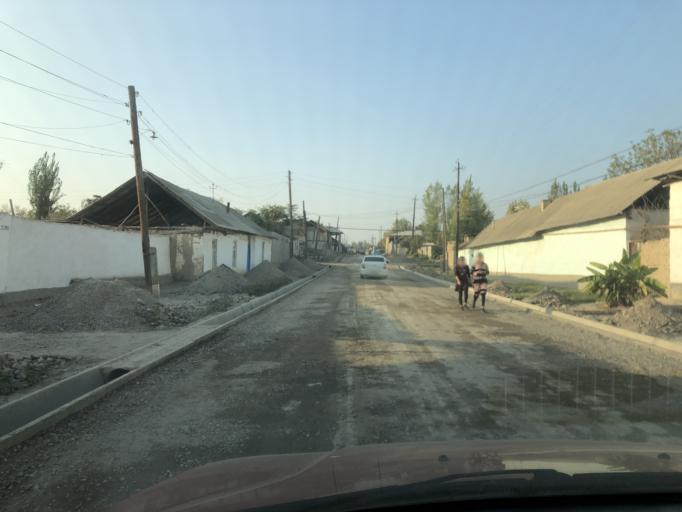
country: UZ
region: Namangan
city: Uychi
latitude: 41.0804
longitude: 72.0004
